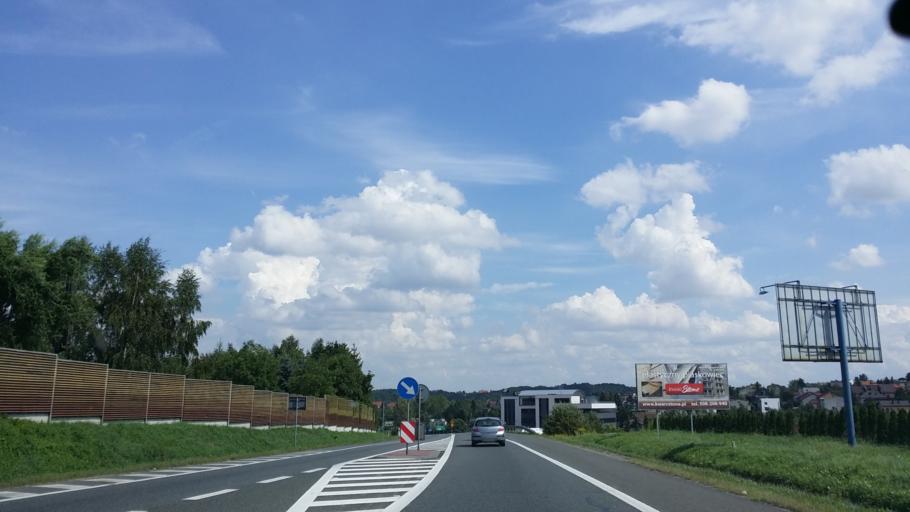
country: PL
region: Lesser Poland Voivodeship
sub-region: Powiat wielicki
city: Wieliczka
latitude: 49.9946
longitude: 20.0682
